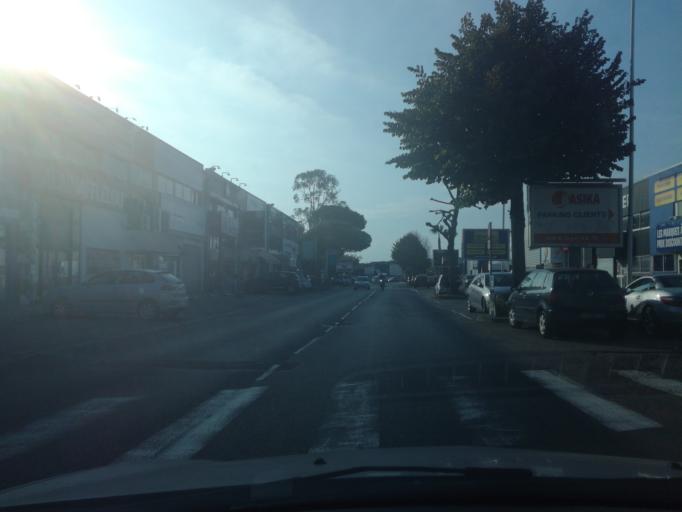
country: FR
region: Provence-Alpes-Cote d'Azur
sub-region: Departement des Alpes-Maritimes
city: Mandelieu-la-Napoule
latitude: 43.5547
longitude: 6.9556
